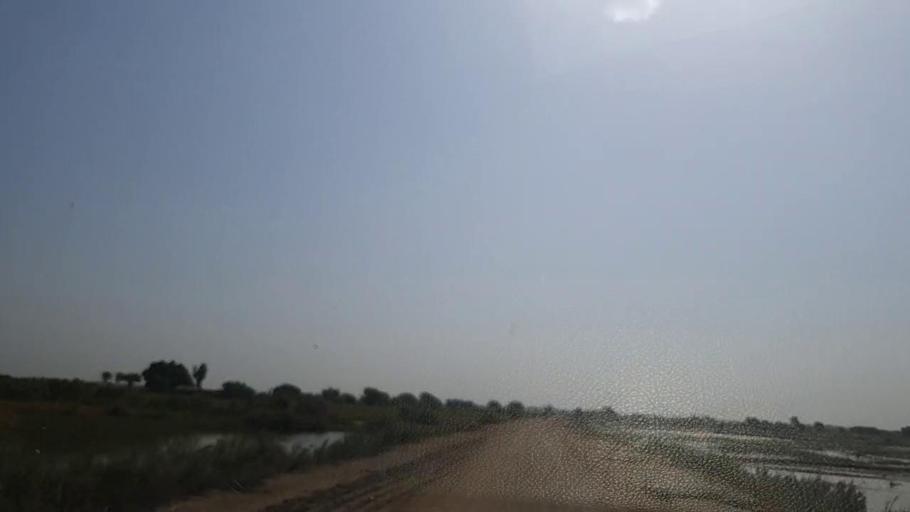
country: PK
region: Sindh
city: Daro Mehar
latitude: 24.7089
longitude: 68.1245
